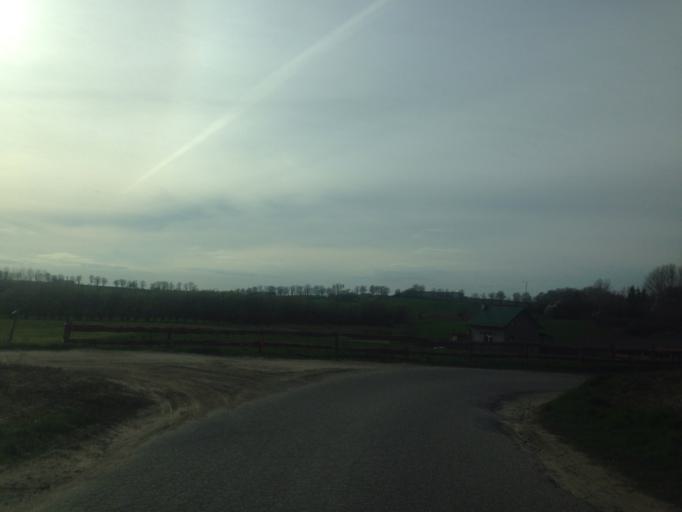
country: PL
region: Kujawsko-Pomorskie
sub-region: Powiat brodnicki
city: Jablonowo Pomorskie
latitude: 53.4233
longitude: 19.2042
